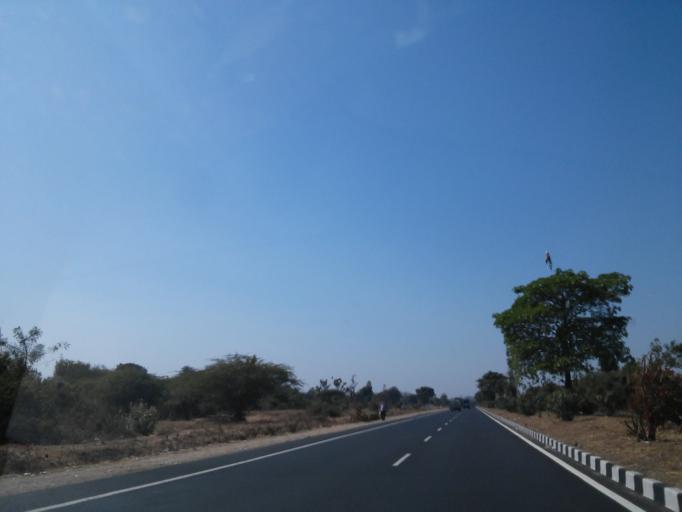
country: IN
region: Gujarat
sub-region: Sabar Kantha
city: Himatnagar
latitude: 23.5998
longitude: 73.1571
